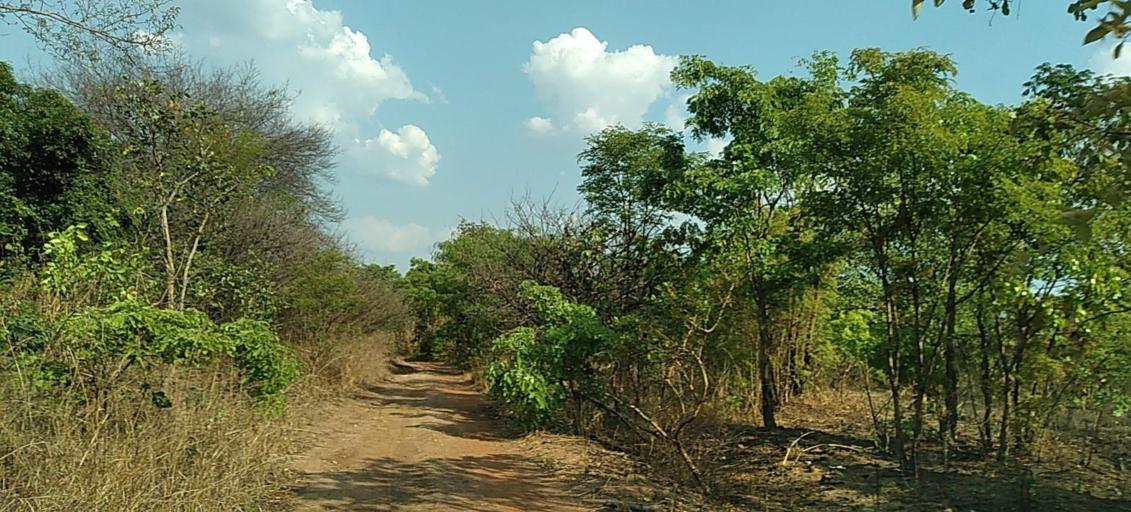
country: ZM
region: Copperbelt
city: Luanshya
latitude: -13.1651
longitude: 28.3453
